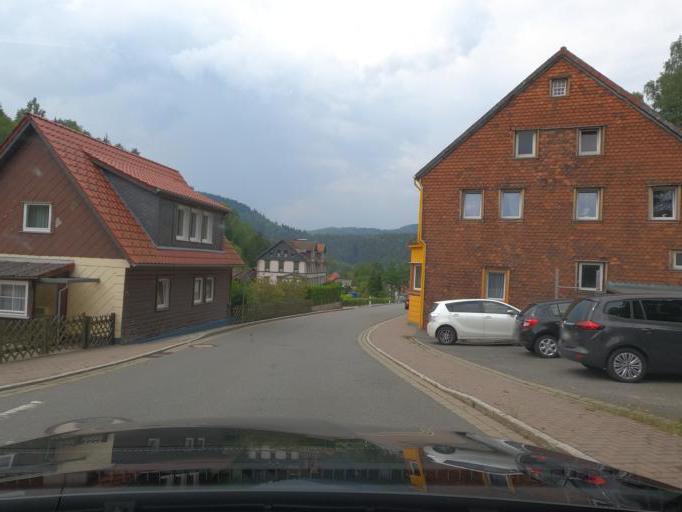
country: DE
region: Lower Saxony
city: Wildemann
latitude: 51.8651
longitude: 10.2949
